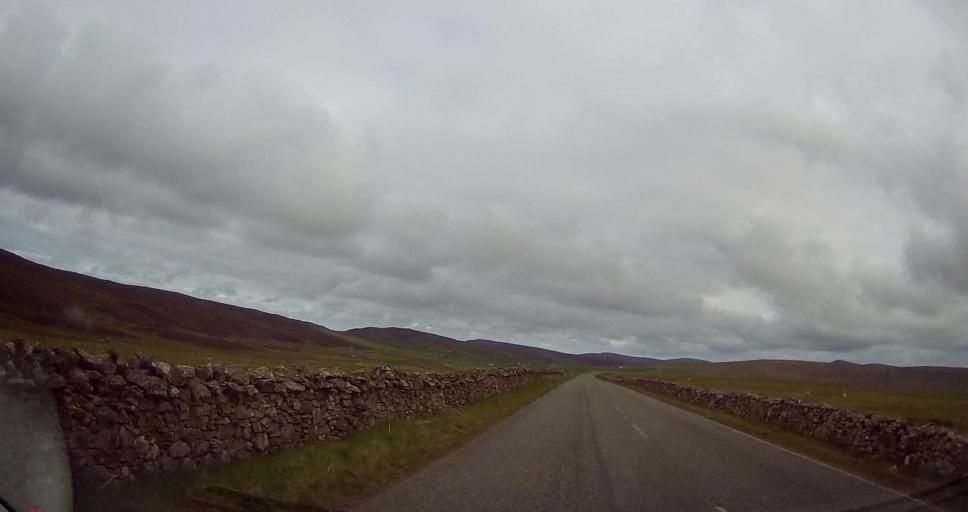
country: GB
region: Scotland
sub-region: Shetland Islands
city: Shetland
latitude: 60.7454
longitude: -0.8843
